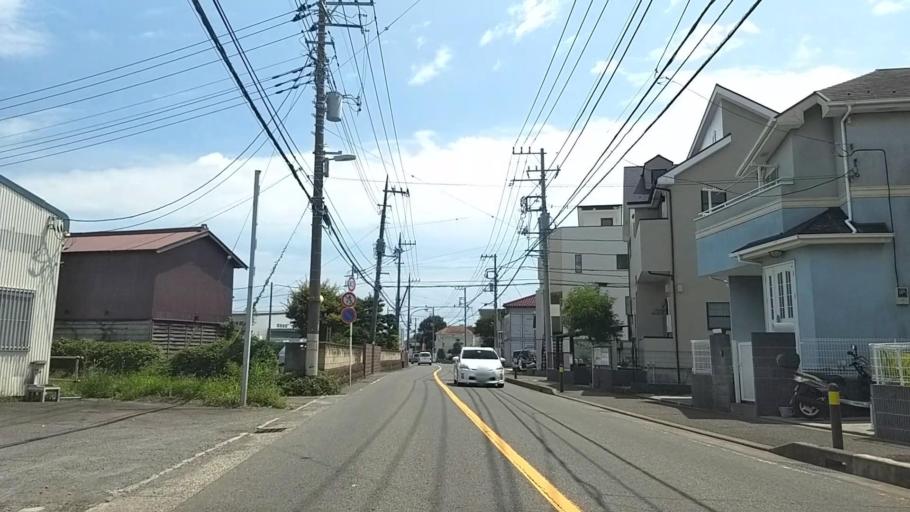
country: JP
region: Kanagawa
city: Fujisawa
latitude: 35.3959
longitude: 139.4408
